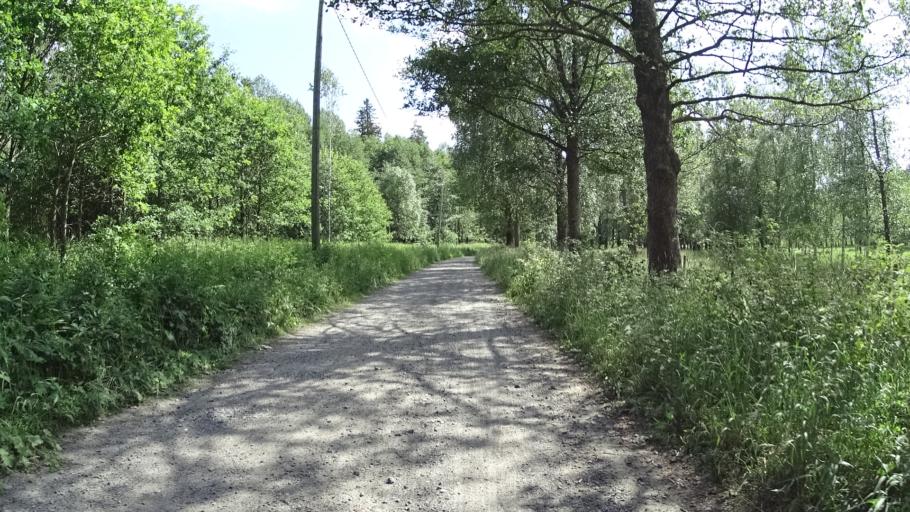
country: FI
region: Uusimaa
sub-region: Raaseporin
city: Pohja
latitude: 60.1226
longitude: 23.5385
